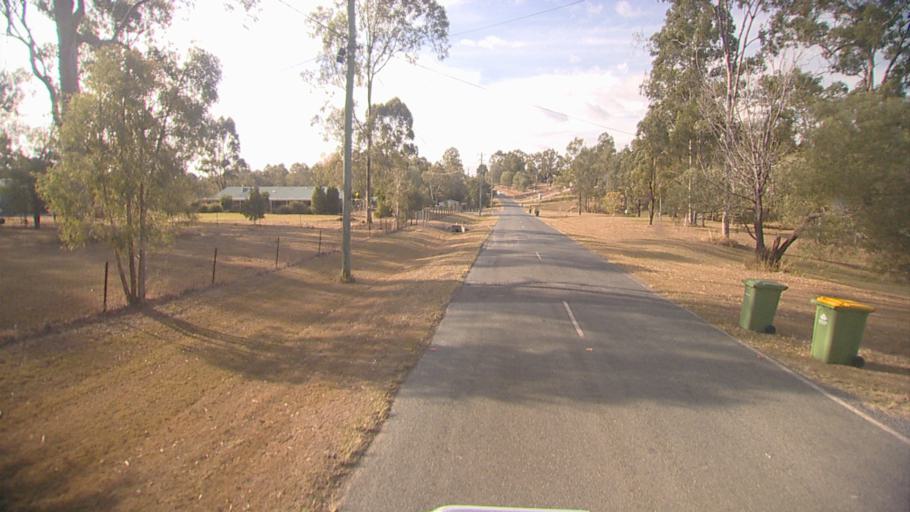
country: AU
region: Queensland
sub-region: Logan
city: Cedar Vale
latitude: -27.8783
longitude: 153.0012
